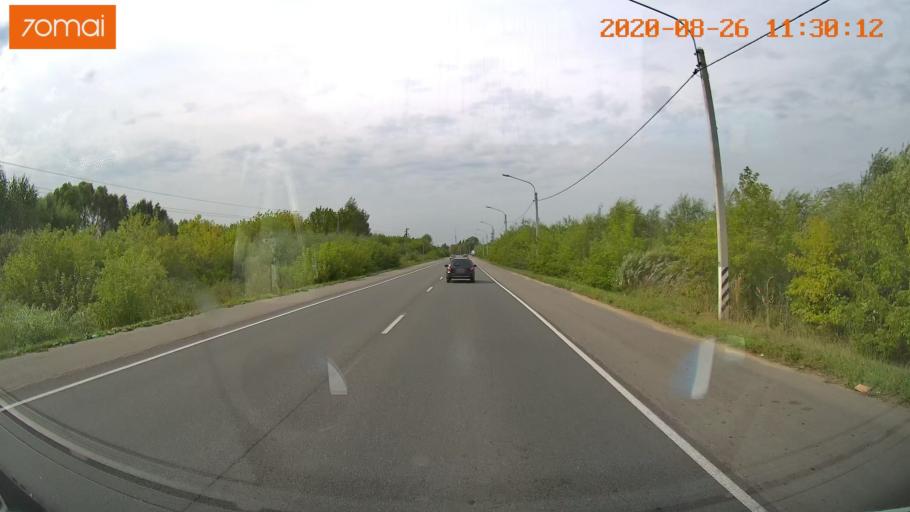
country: RU
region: Rjazan
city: Shilovo
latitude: 54.3163
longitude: 40.8875
